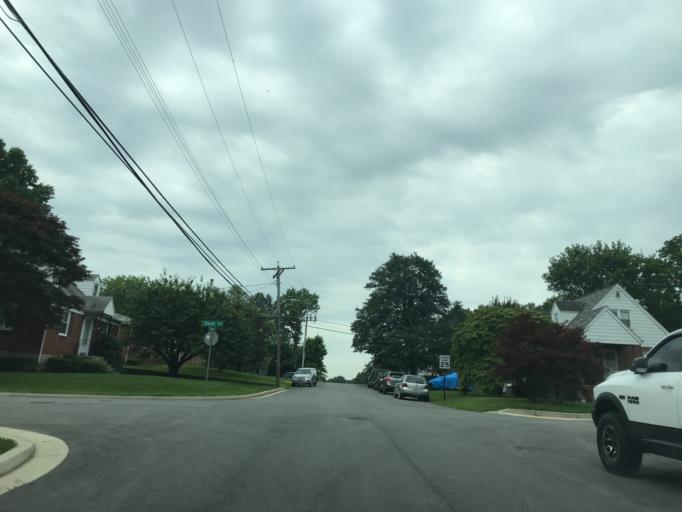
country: US
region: Maryland
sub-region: Baltimore County
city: Overlea
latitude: 39.3625
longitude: -76.5119
